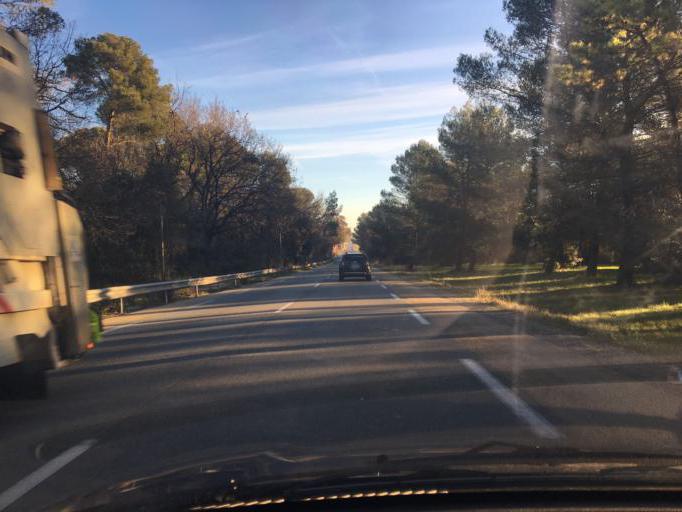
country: FR
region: Provence-Alpes-Cote d'Azur
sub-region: Departement du Var
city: La Motte
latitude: 43.4605
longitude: 6.5256
